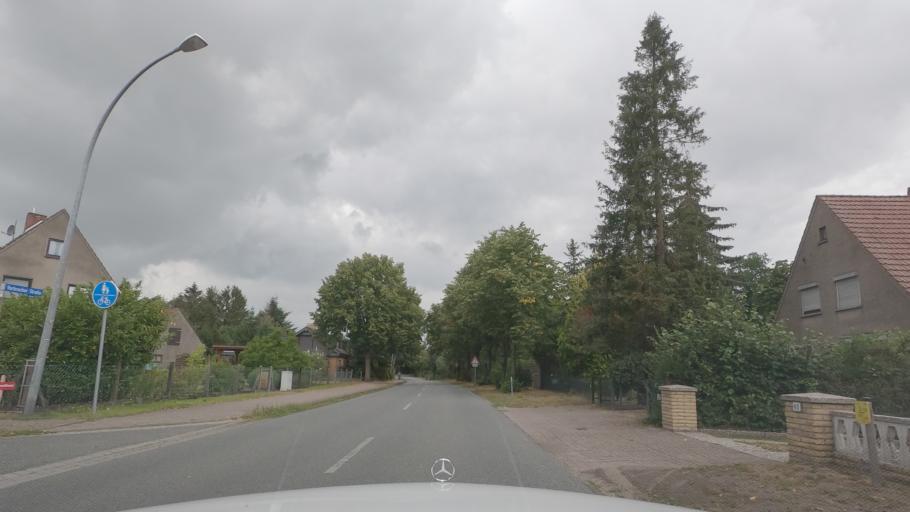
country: DE
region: Lower Saxony
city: Neuenkirchen
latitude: 53.2302
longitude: 8.5293
